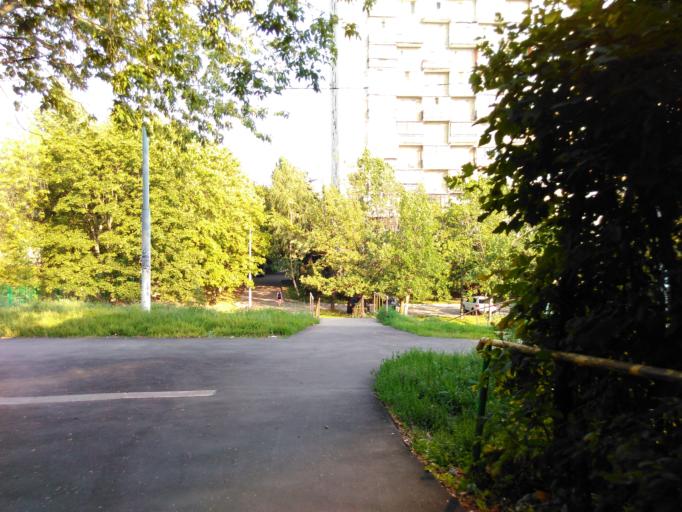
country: RU
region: Moscow
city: Zyuzino
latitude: 55.6420
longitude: 37.5447
